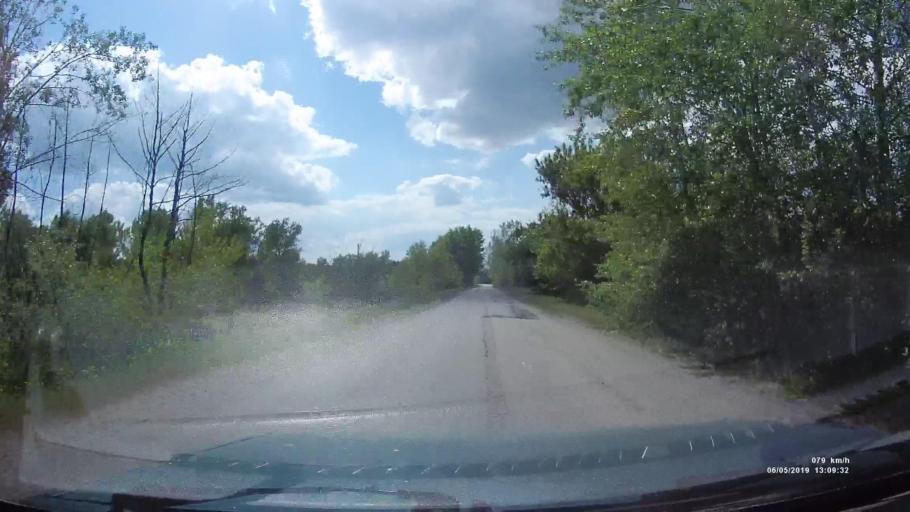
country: RU
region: Rostov
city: Ust'-Donetskiy
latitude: 47.7676
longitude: 40.9827
